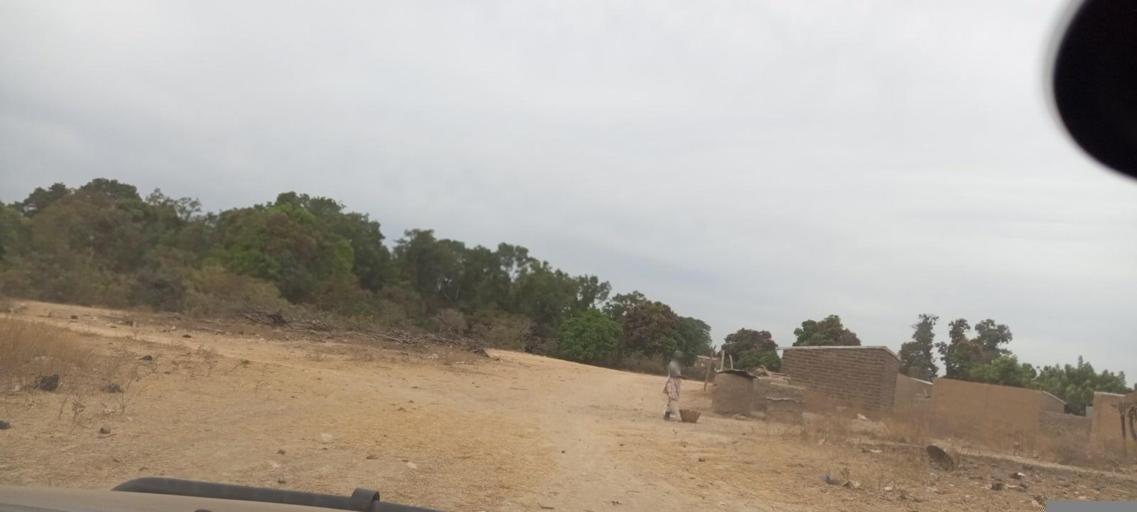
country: ML
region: Koulikoro
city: Kati
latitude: 12.7430
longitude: -8.3303
